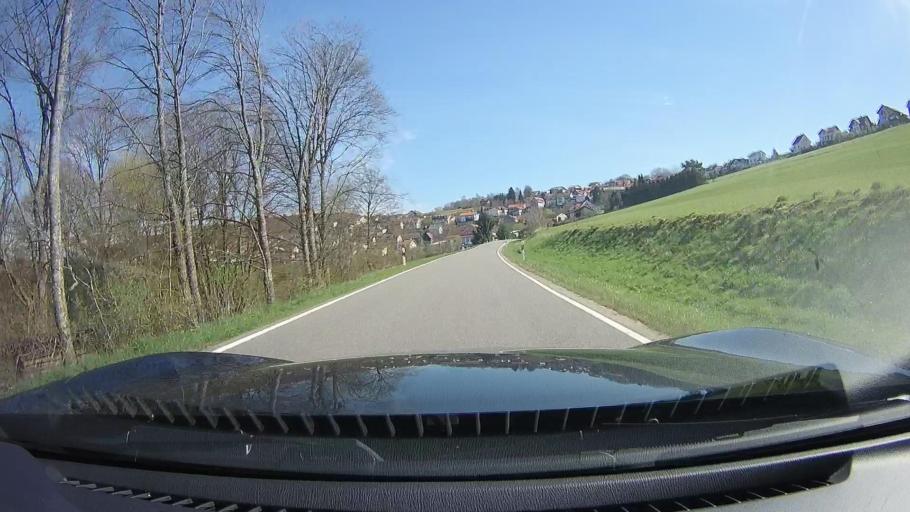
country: DE
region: Hesse
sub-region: Regierungsbezirk Darmstadt
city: Rothenberg
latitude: 49.4955
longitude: 8.9163
